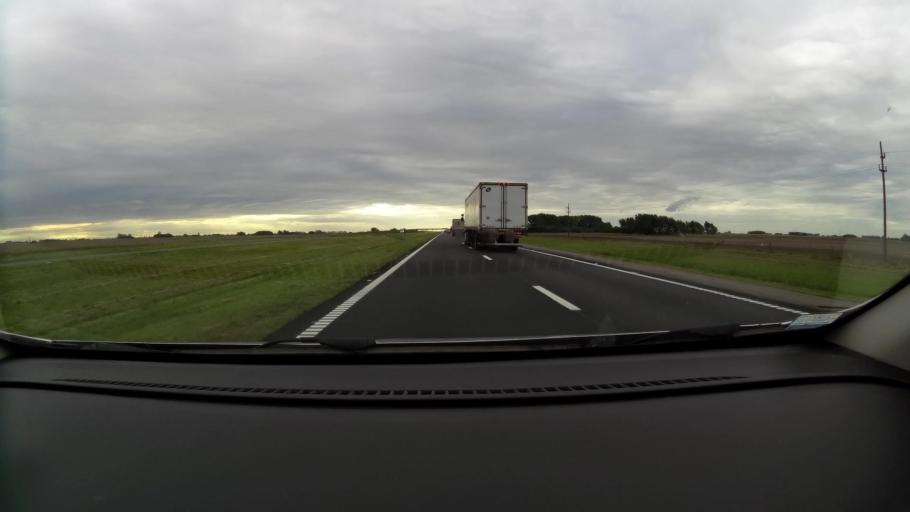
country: AR
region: Buenos Aires
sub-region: Partido de Ramallo
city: Ramallo
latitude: -33.6113
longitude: -60.0173
